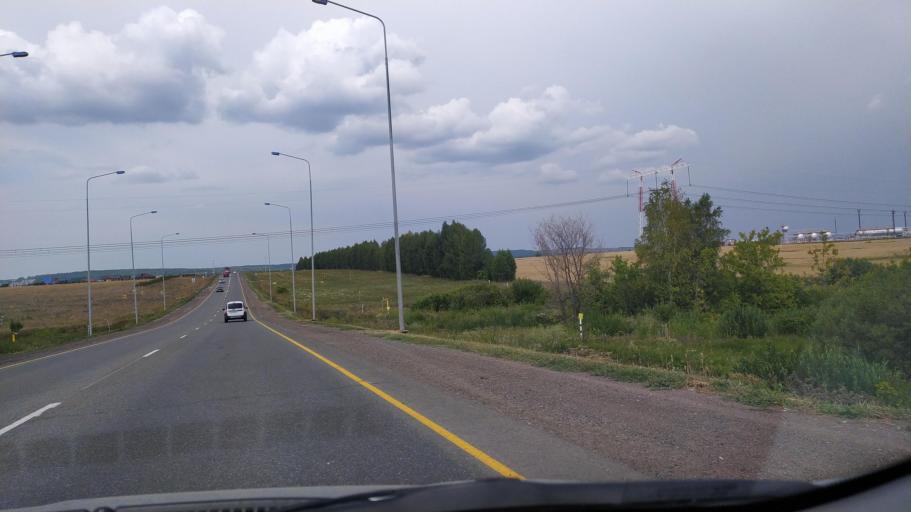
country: RU
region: Tatarstan
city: Al'met'yevsk
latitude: 54.9014
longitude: 52.2206
